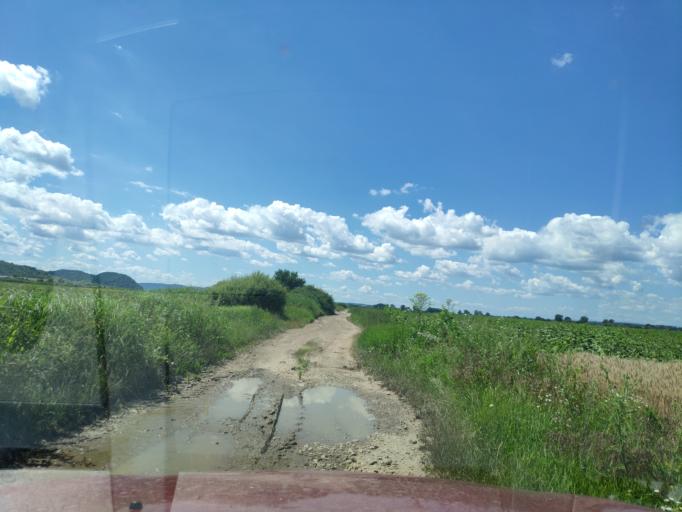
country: HU
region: Borsod-Abauj-Zemplen
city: Ozd
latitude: 48.2854
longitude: 20.2055
